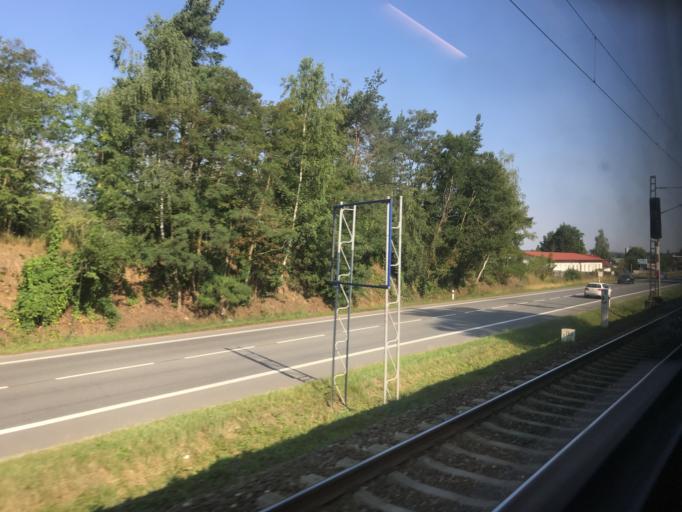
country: CZ
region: Jihocesky
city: Plana nad Luznici
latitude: 49.3429
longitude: 14.7109
